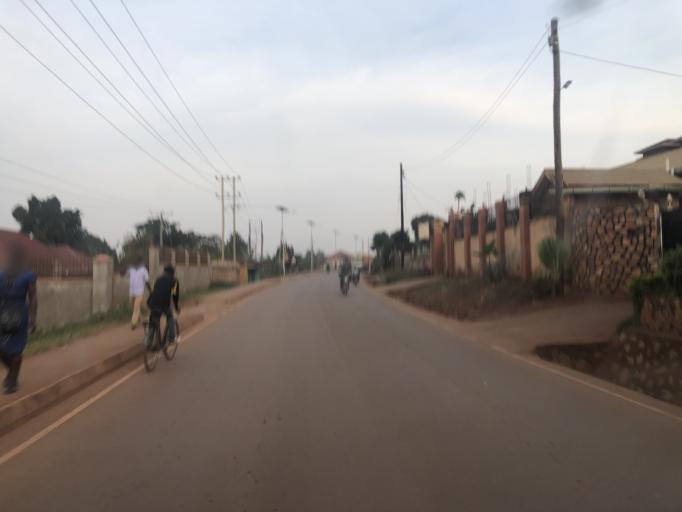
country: UG
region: Central Region
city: Kampala Central Division
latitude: 0.2909
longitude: 32.5354
